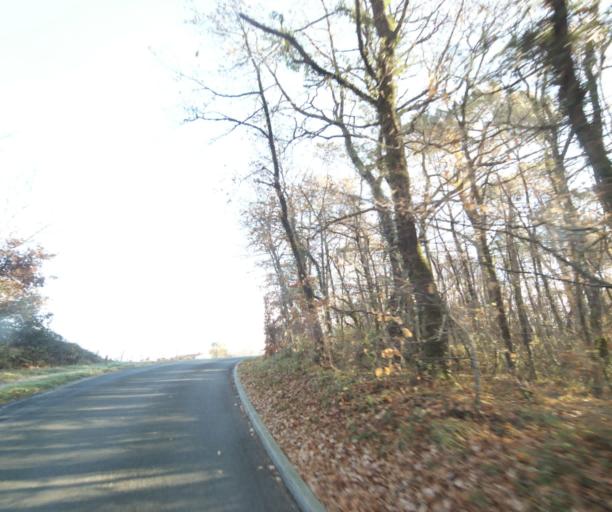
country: FR
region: Poitou-Charentes
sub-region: Departement de la Charente-Maritime
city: Fontcouverte
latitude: 45.7669
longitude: -0.5996
